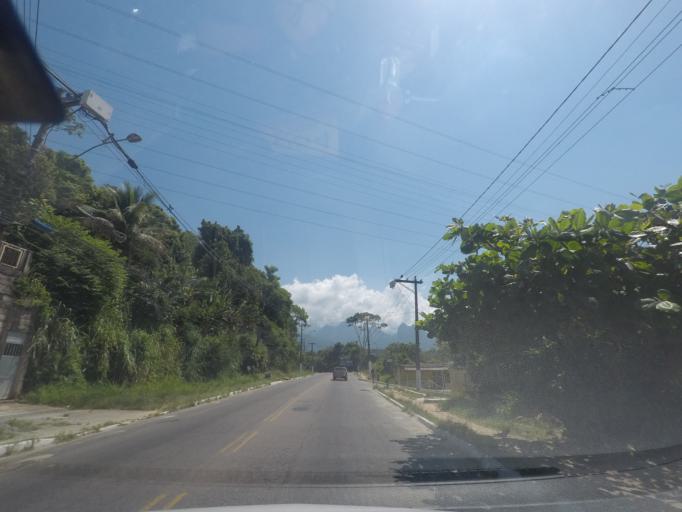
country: BR
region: Rio de Janeiro
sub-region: Petropolis
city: Petropolis
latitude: -22.6008
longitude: -43.1882
